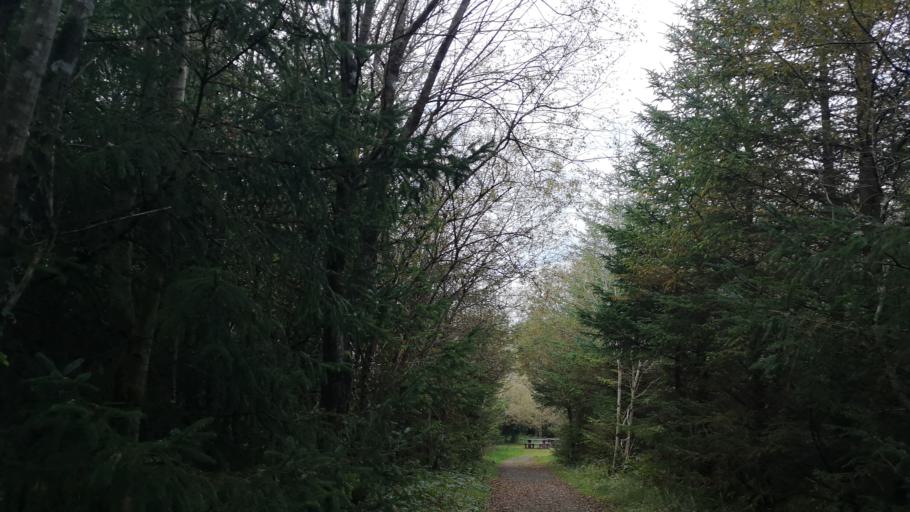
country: IE
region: Connaught
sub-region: County Galway
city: Loughrea
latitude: 53.2388
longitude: -8.6500
